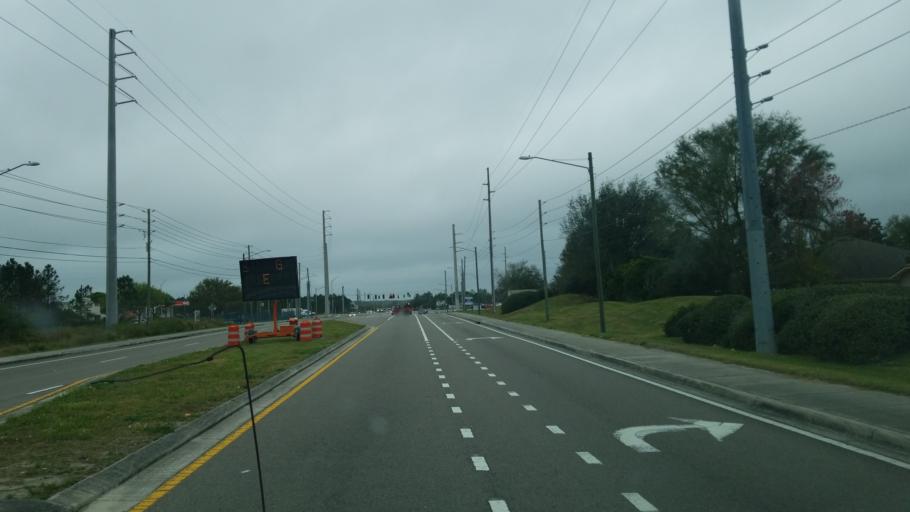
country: US
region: Florida
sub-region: Lake County
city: Four Corners
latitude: 28.2547
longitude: -81.6558
